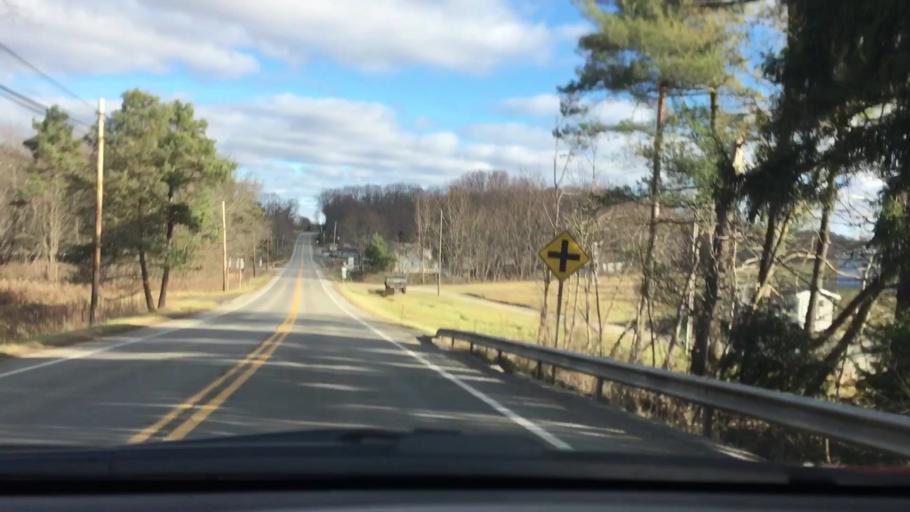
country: US
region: Pennsylvania
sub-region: Westmoreland County
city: Avonmore
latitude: 40.6103
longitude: -79.4386
